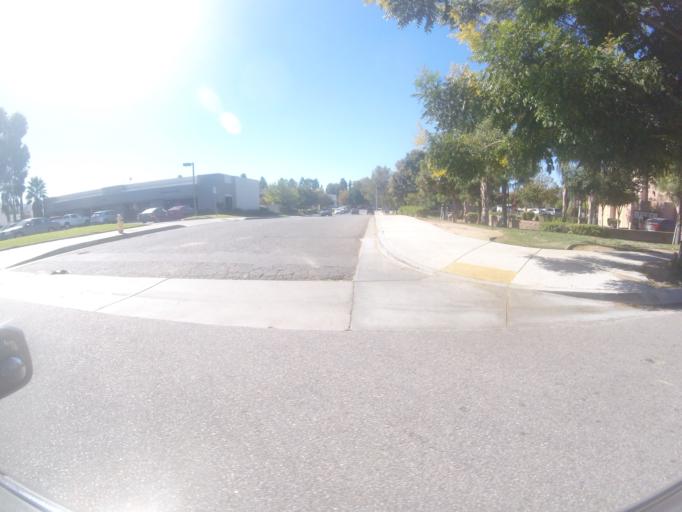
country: US
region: California
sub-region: San Bernardino County
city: Redlands
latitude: 34.0623
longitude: -117.2218
